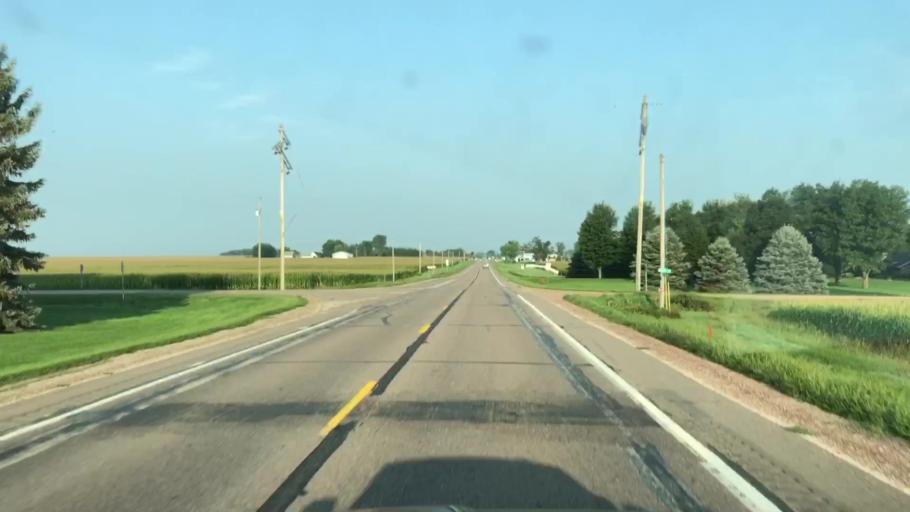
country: US
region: Iowa
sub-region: O'Brien County
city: Sheldon
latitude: 43.1863
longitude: -95.9795
